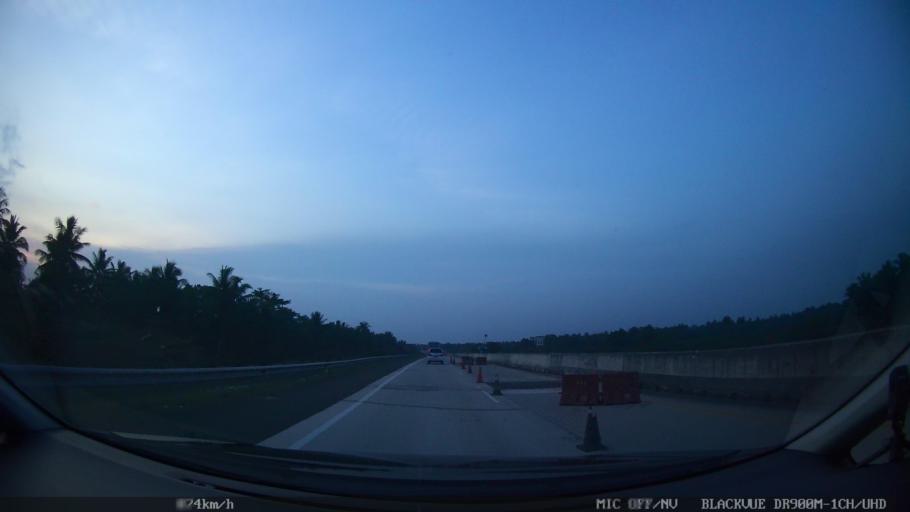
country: ID
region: Lampung
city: Kalianda
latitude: -5.6610
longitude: 105.5913
